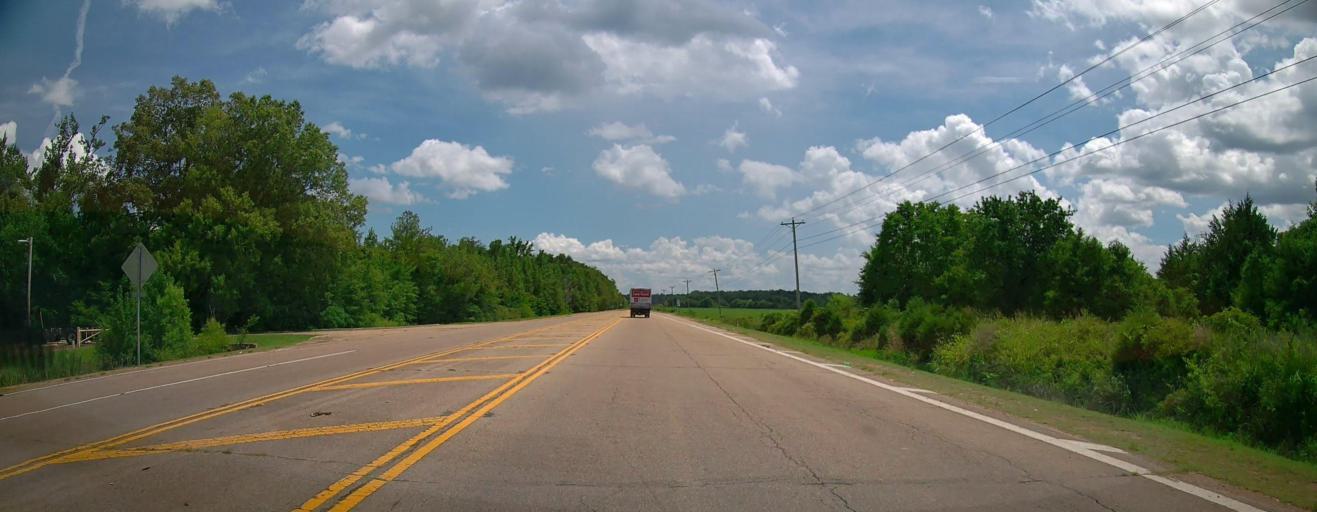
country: US
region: Mississippi
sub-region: Lee County
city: Shannon
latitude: 34.1509
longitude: -88.7195
